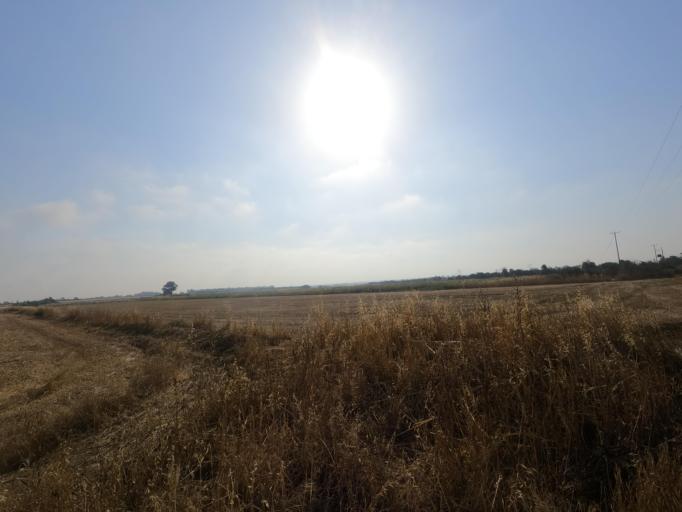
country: CY
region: Ammochostos
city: Avgorou
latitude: 35.0535
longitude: 33.8177
